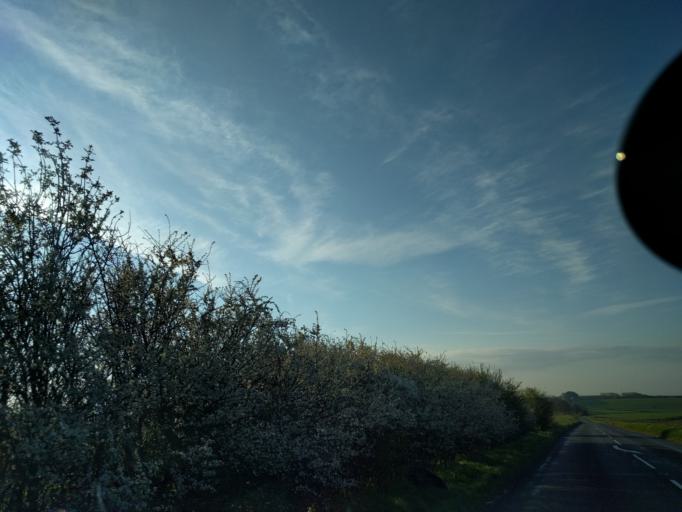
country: GB
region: England
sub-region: Wiltshire
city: Woodford
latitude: 51.1146
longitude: -1.8498
